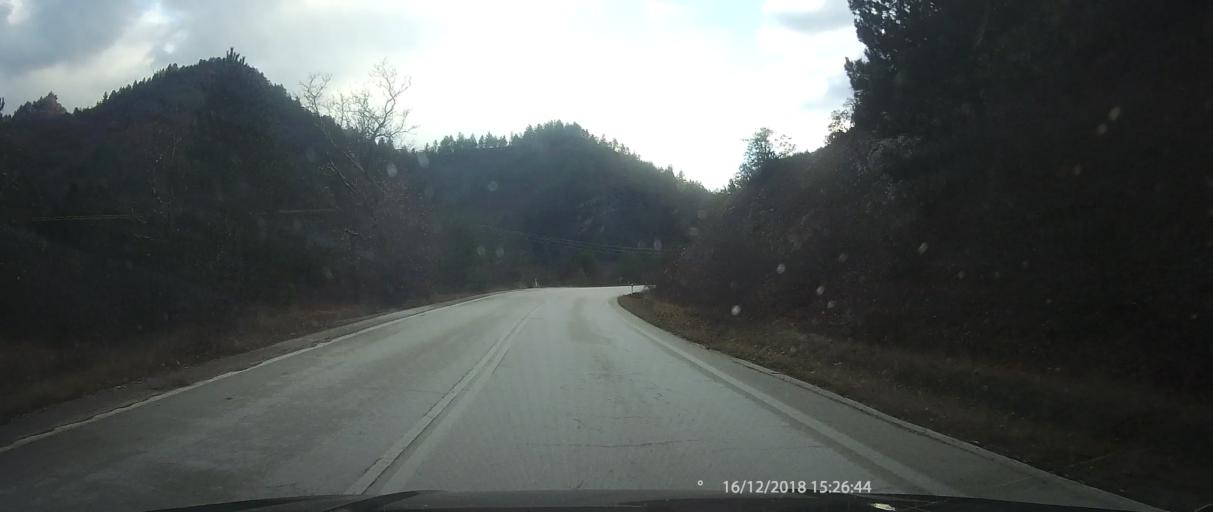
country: GR
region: Epirus
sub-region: Nomos Ioanninon
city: Konitsa
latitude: 40.1145
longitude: 20.7768
